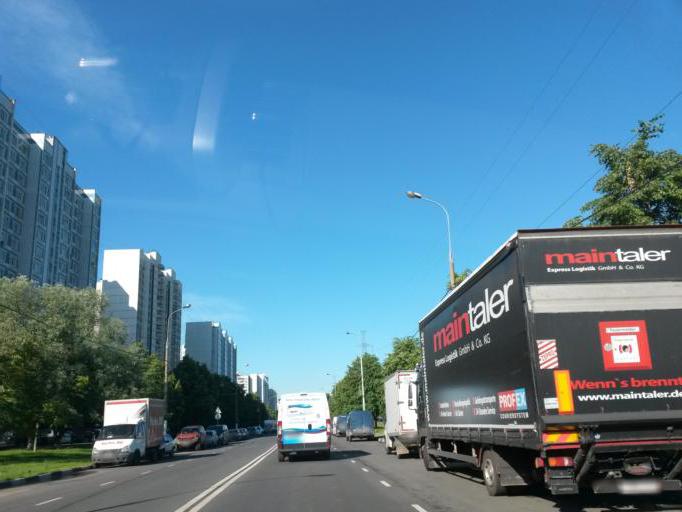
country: RU
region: Moscow
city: Brateyevo
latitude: 55.6425
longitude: 37.7643
